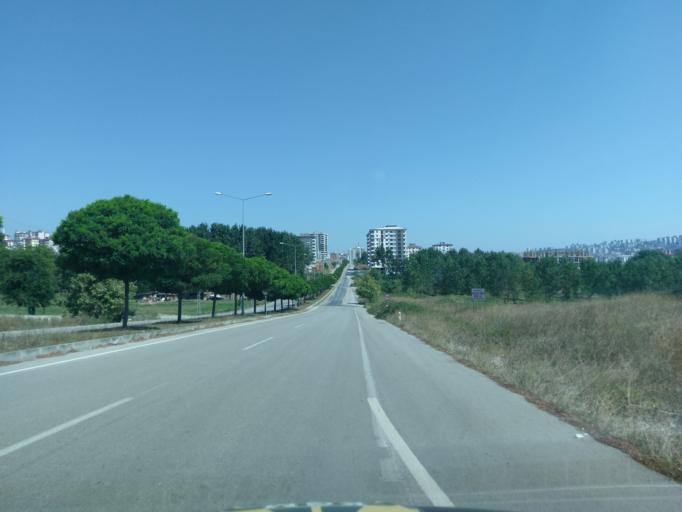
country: TR
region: Samsun
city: Samsun
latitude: 41.2579
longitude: 36.3089
